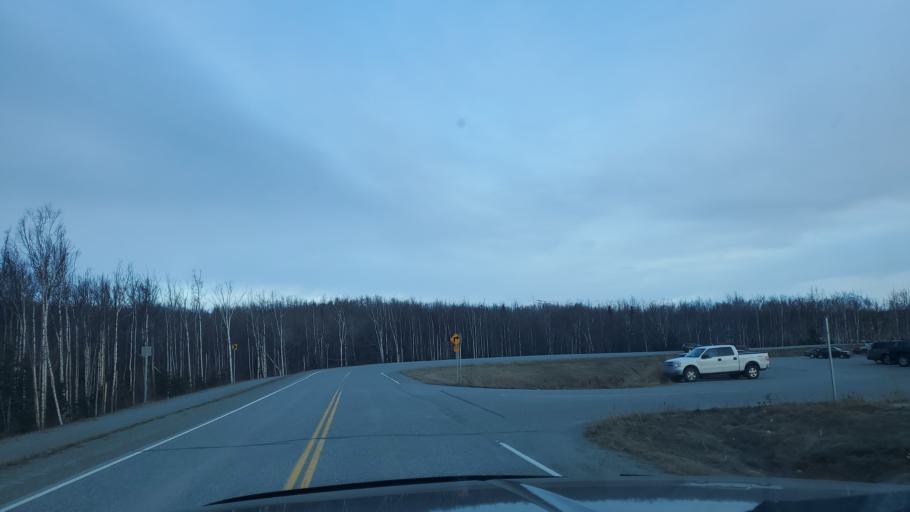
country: US
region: Alaska
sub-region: Matanuska-Susitna Borough
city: Gateway
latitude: 61.5654
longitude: -149.2652
